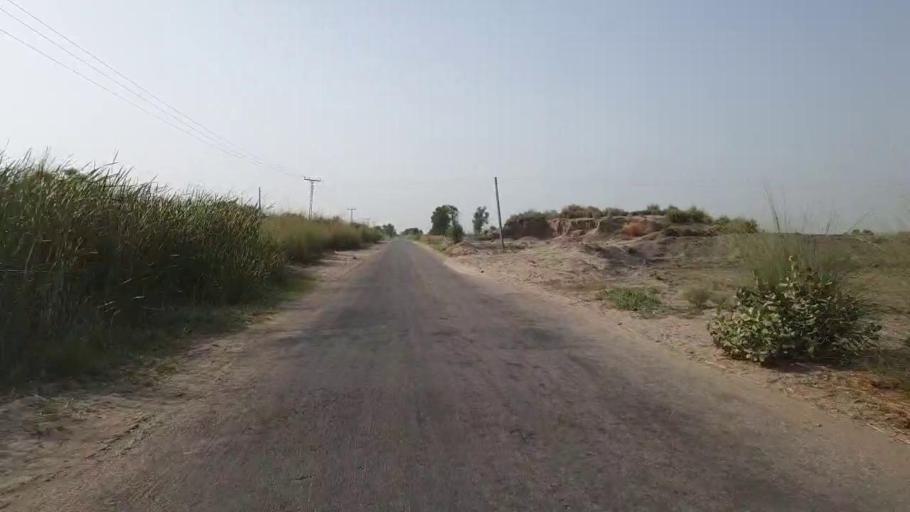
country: PK
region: Sindh
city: Khadro
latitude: 26.3556
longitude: 68.9211
